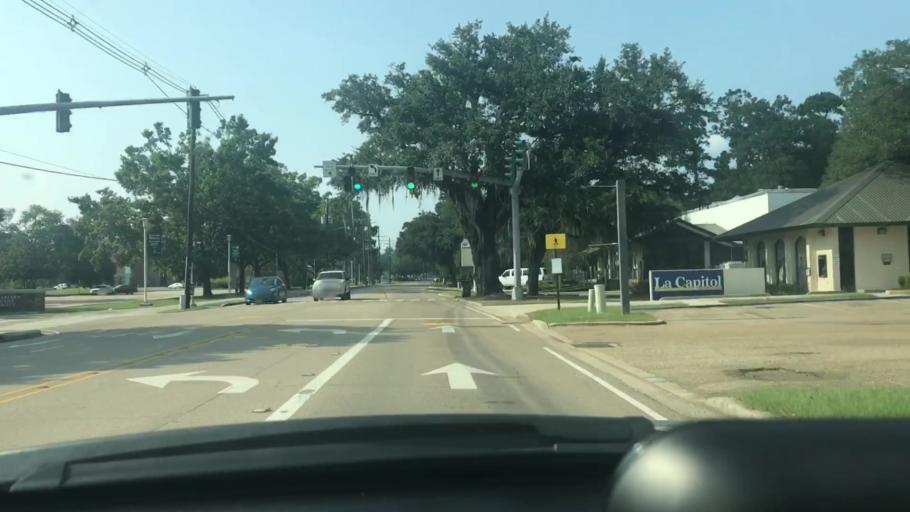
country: US
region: Louisiana
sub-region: Tangipahoa Parish
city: Hammond
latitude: 30.5124
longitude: -90.4650
